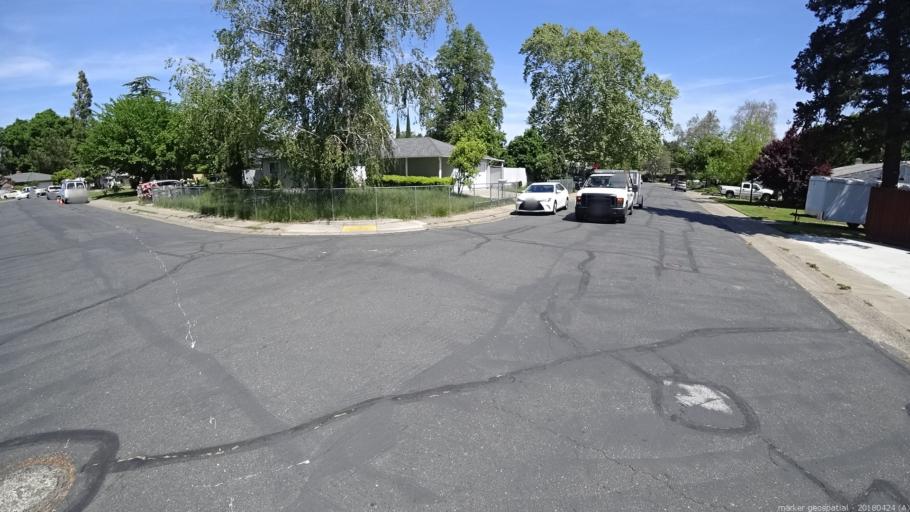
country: US
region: California
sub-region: Yolo County
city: West Sacramento
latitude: 38.5745
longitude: -121.5294
